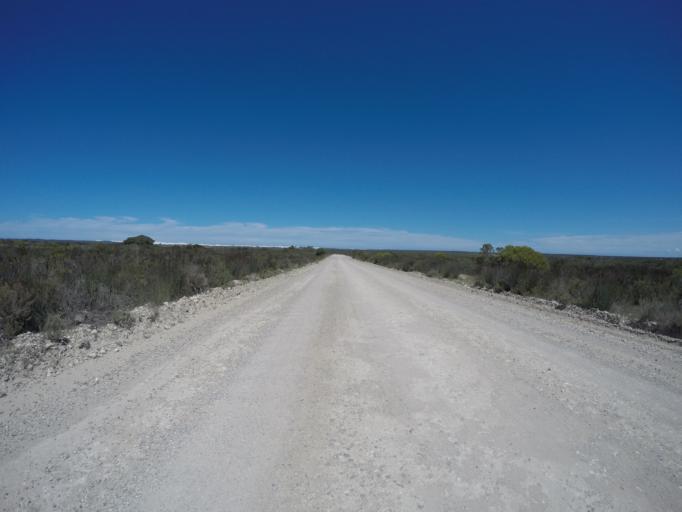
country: ZA
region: Western Cape
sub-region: Overberg District Municipality
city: Bredasdorp
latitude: -34.4428
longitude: 20.4215
